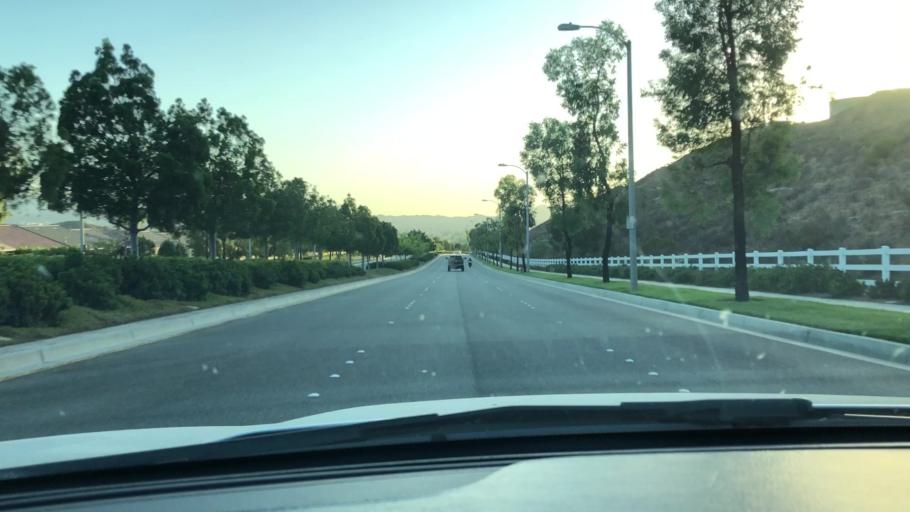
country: US
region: California
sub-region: Los Angeles County
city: Santa Clarita
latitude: 34.4252
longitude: -118.5220
